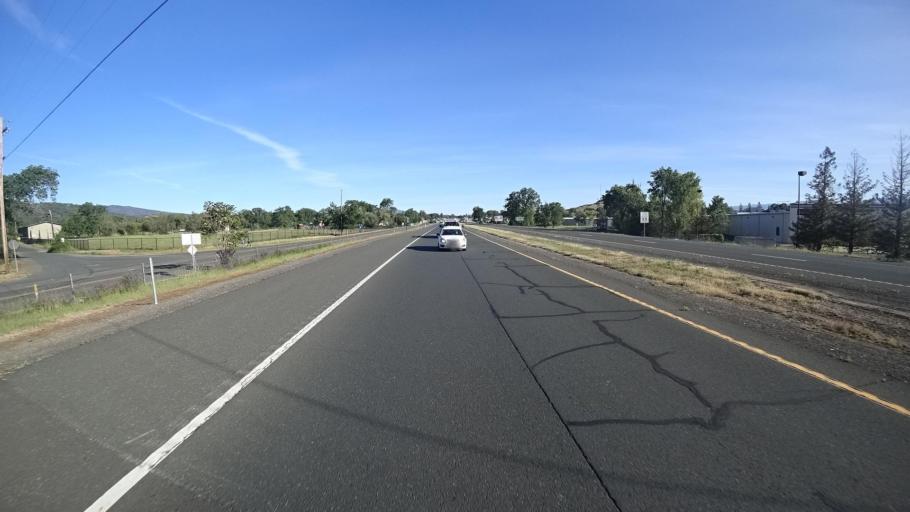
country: US
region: California
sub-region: Lake County
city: Lakeport
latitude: 39.0259
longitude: -122.9191
